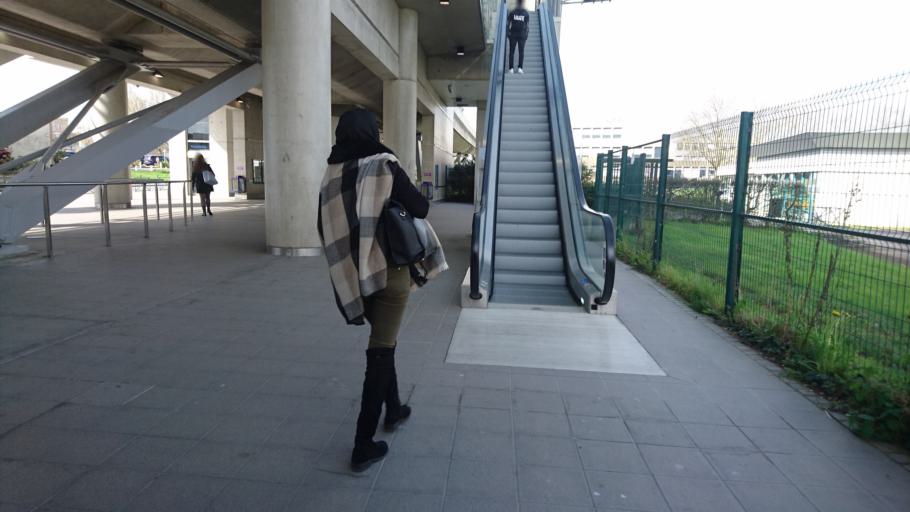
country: FR
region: Brittany
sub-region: Departement d'Ille-et-Vilaine
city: Rennes
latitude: 48.1217
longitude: -1.6932
